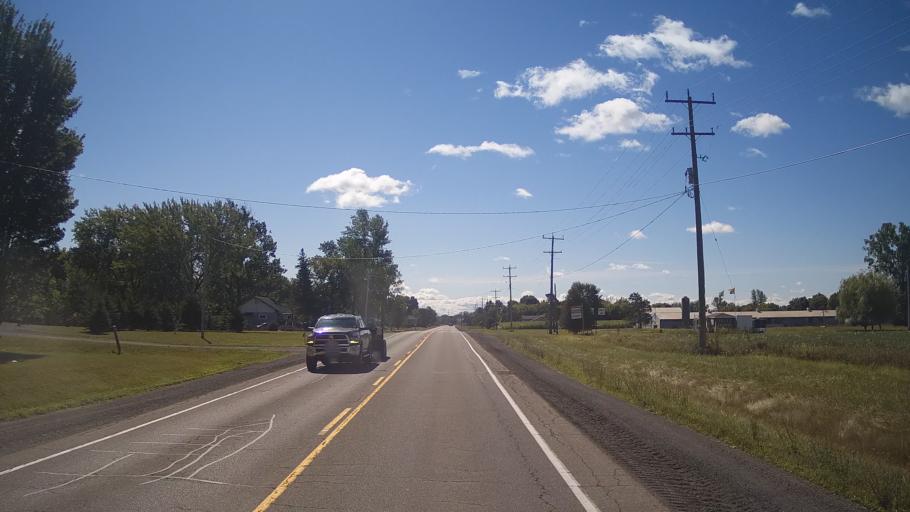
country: US
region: New York
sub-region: St. Lawrence County
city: Norfolk
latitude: 44.9410
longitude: -75.2168
